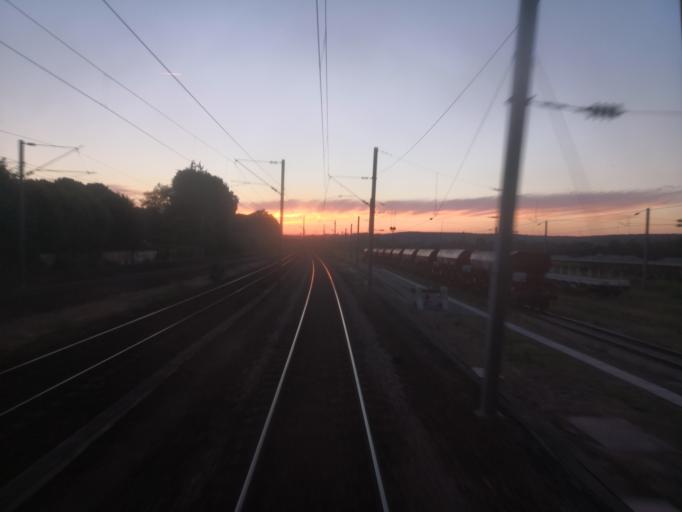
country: FR
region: Ile-de-France
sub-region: Departement des Yvelines
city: Vernouillet
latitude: 48.9827
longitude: 1.9814
